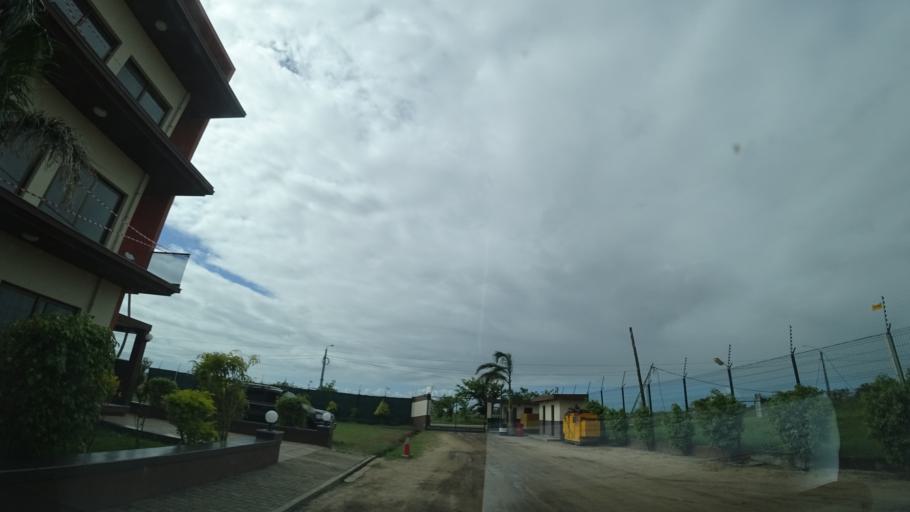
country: MZ
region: Sofala
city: Beira
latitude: -19.8029
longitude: 34.9016
